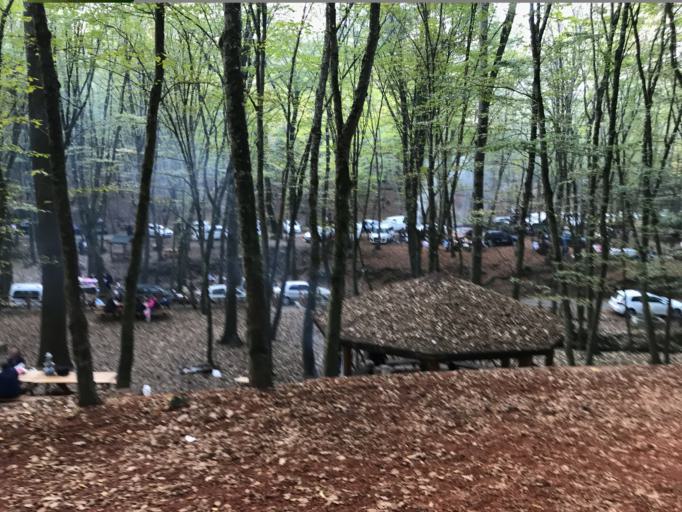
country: TR
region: Istanbul
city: Kemerburgaz
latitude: 41.1733
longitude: 28.9577
